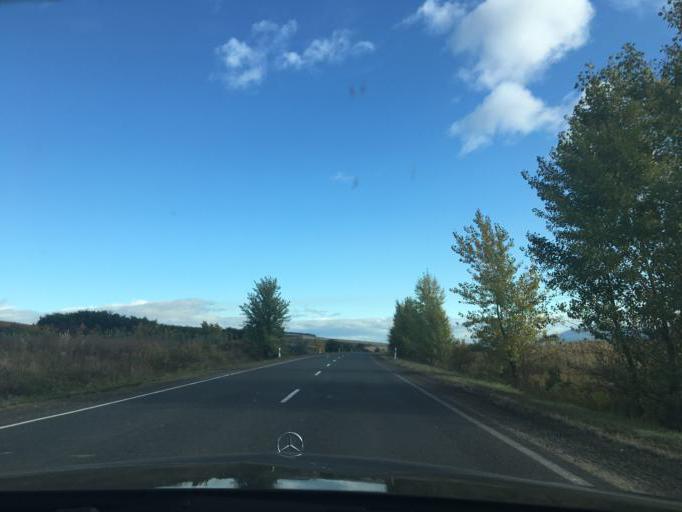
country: HU
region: Borsod-Abauj-Zemplen
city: Gonc
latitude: 48.5043
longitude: 21.2230
